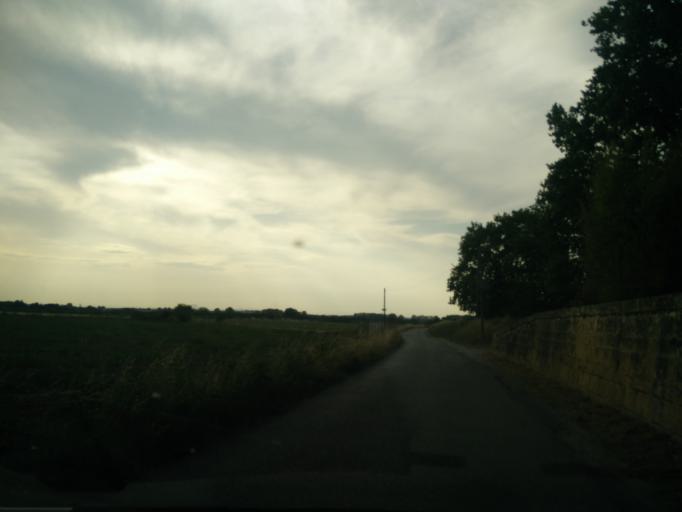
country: FR
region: Languedoc-Roussillon
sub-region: Departement de l'Herault
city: Marsillargues
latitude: 43.6809
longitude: 4.1704
